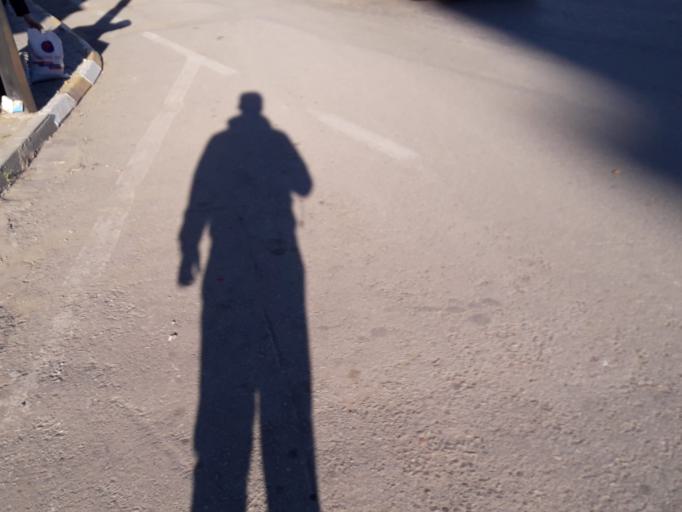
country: TR
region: Sinop
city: Sinop
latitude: 42.0219
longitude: 35.1354
